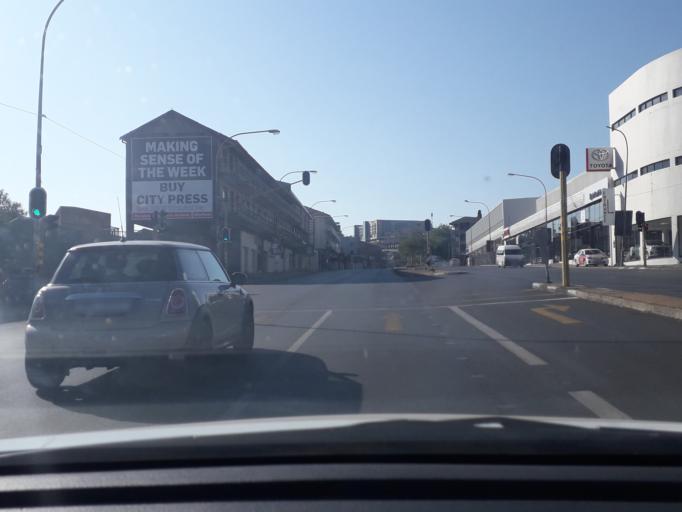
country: ZA
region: Gauteng
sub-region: City of Johannesburg Metropolitan Municipality
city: Johannesburg
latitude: -26.1194
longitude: 28.0273
